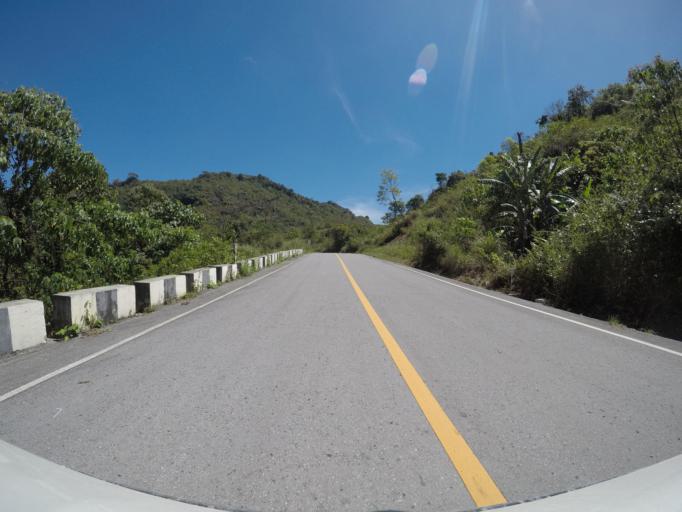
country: TL
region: Manatuto
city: Manatuto
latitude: -8.7672
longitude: 125.9673
